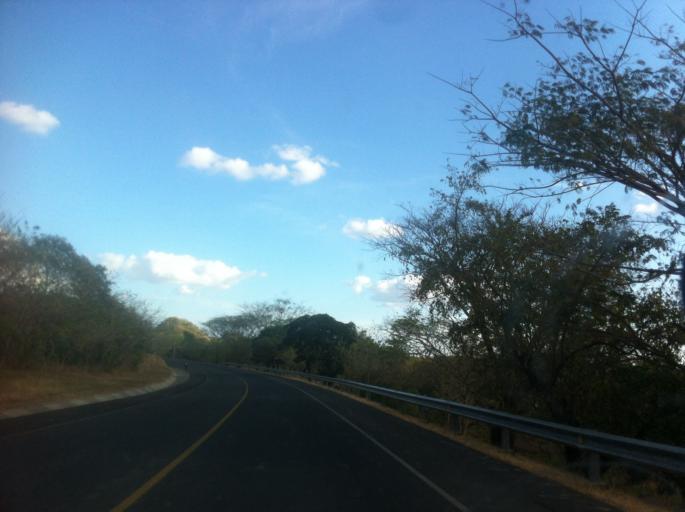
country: NI
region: Chontales
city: Acoyapa
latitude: 11.9542
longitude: -85.1603
